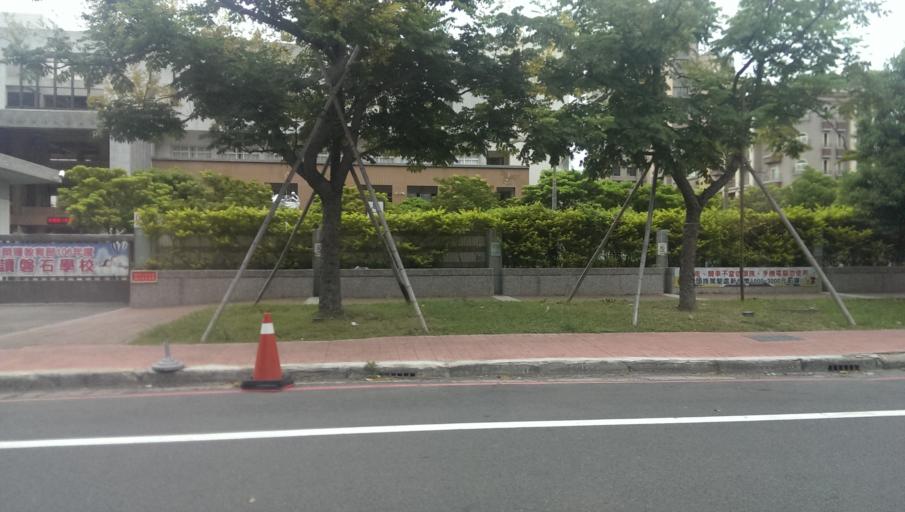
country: TW
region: Taiwan
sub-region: Hsinchu
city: Zhubei
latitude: 24.8181
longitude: 121.0178
